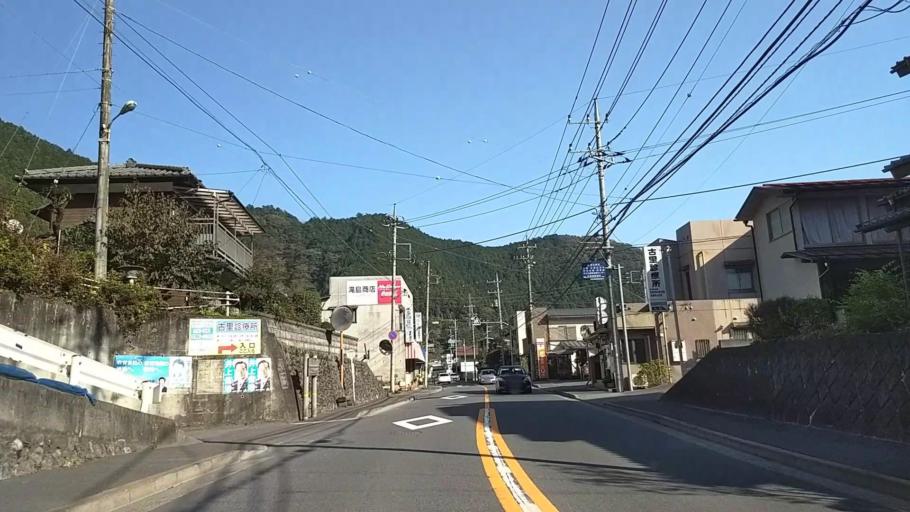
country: JP
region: Tokyo
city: Ome
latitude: 35.8158
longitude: 139.1494
